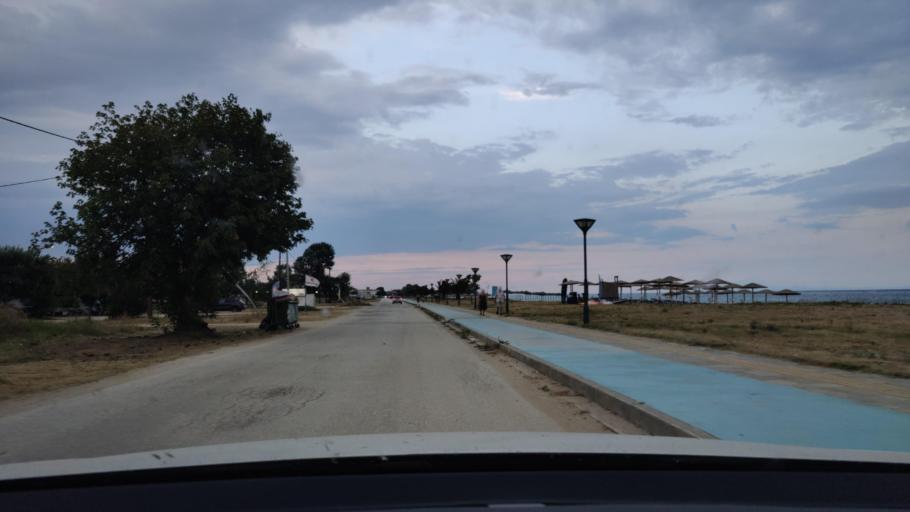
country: GR
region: East Macedonia and Thrace
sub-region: Nomos Kavalas
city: Paralia Ofryniou
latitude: 40.7698
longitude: 23.8903
